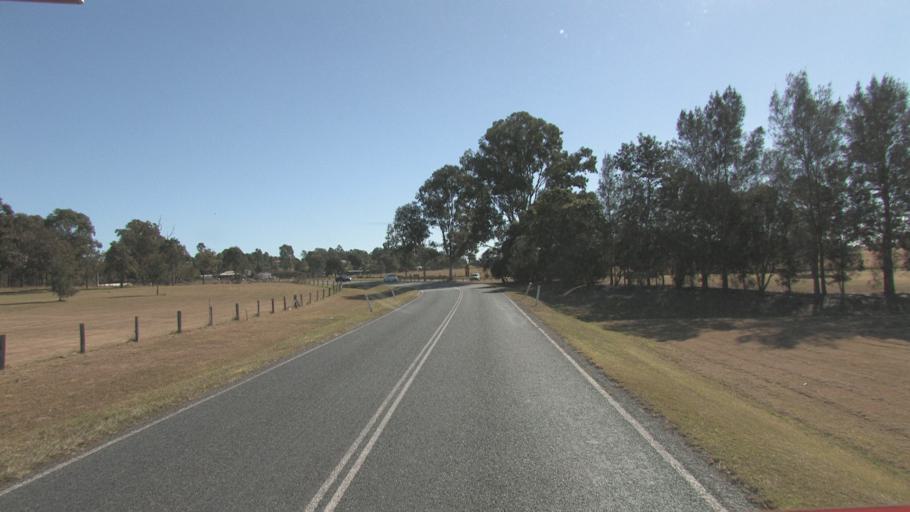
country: AU
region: Queensland
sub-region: Logan
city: Chambers Flat
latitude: -27.7653
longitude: 153.0973
